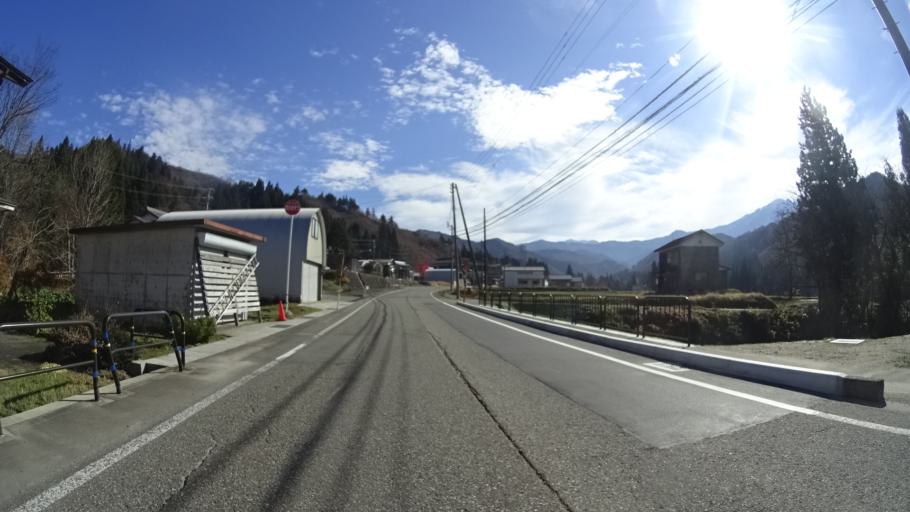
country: JP
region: Niigata
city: Muikamachi
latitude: 37.2037
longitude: 139.0733
